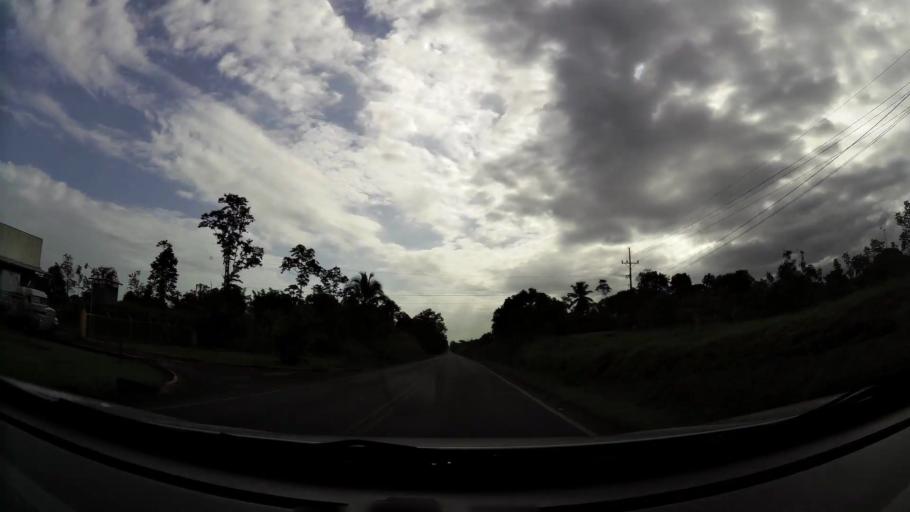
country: CR
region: Limon
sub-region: Canton de Guacimo
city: Guacimo
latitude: 10.2001
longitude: -83.6717
